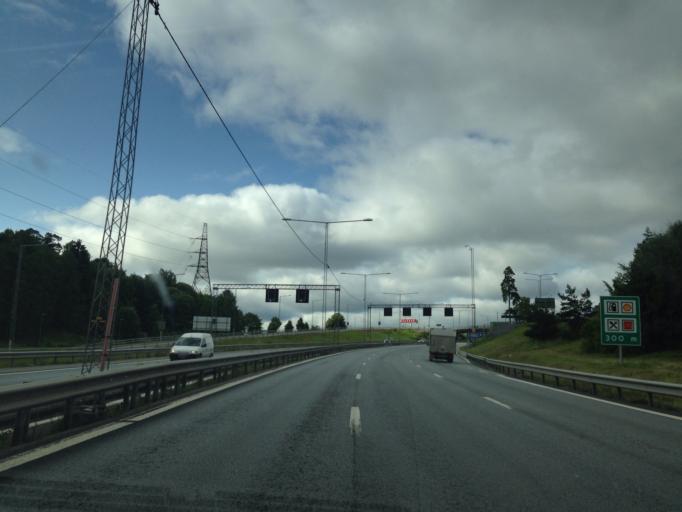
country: SE
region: Stockholm
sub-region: Botkyrka Kommun
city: Alby
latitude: 59.2431
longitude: 17.8380
